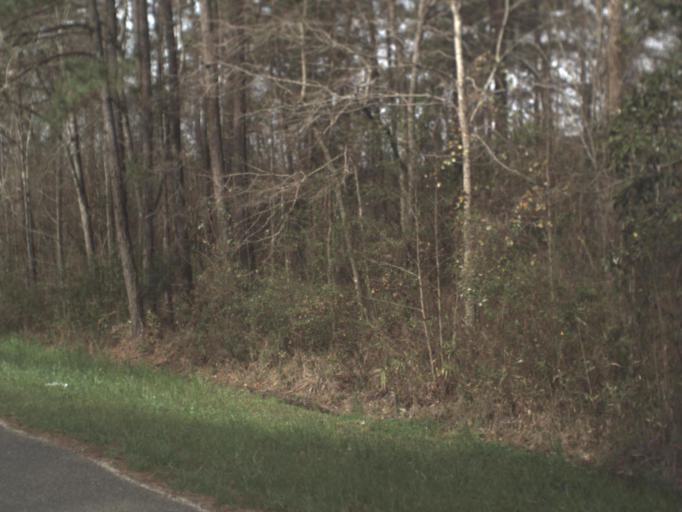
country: US
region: Florida
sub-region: Leon County
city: Tallahassee
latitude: 30.5096
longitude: -84.0868
